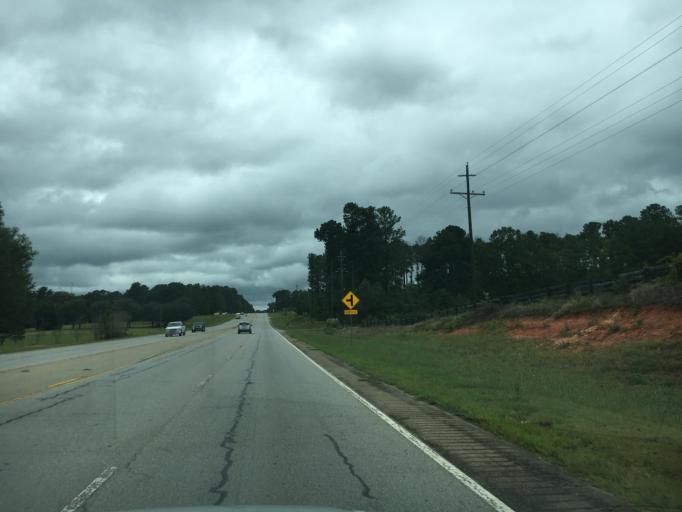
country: US
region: Georgia
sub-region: Wilkes County
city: Washington
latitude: 33.7092
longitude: -82.6980
